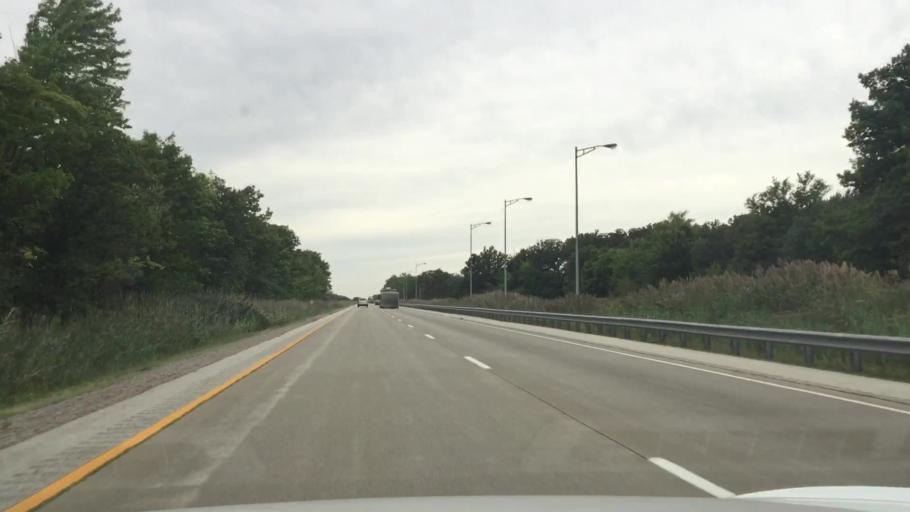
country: CA
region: Ontario
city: Camlachie
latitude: 42.9924
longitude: -82.1705
